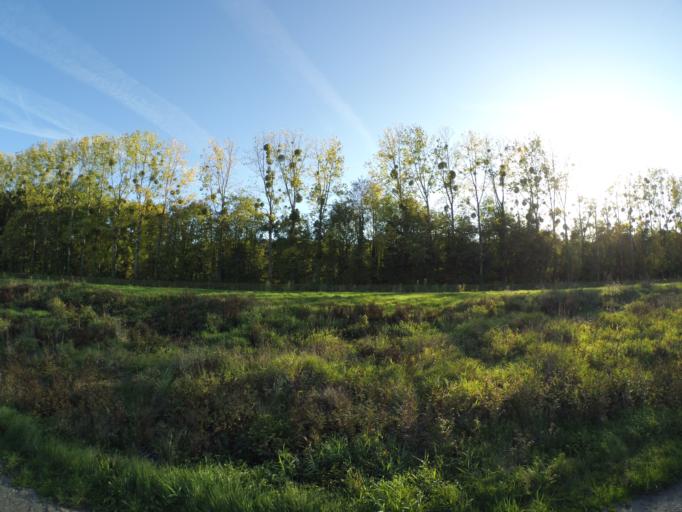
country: FR
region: Brittany
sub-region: Departement du Morbihan
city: Saint-Vincent-sur-Oust
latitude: 47.7198
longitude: -2.1614
